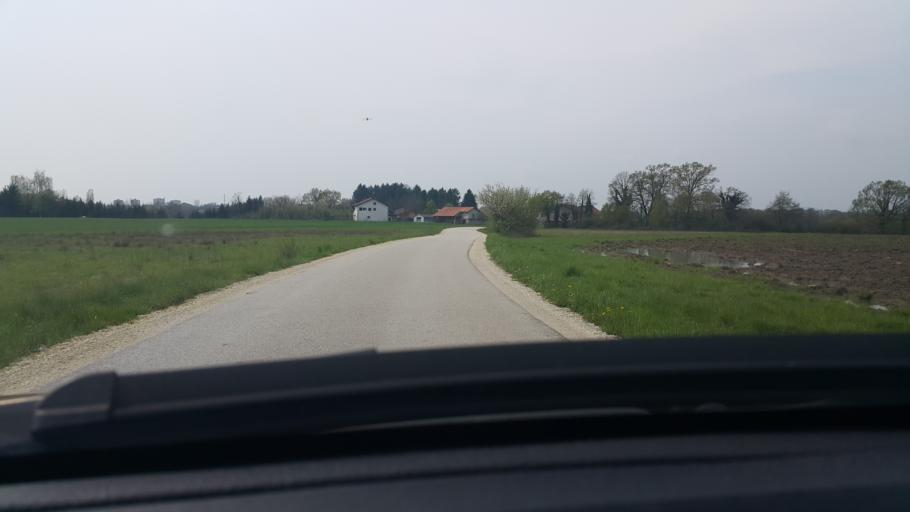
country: SI
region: Brezice
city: Brezice
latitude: 45.9112
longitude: 15.6253
